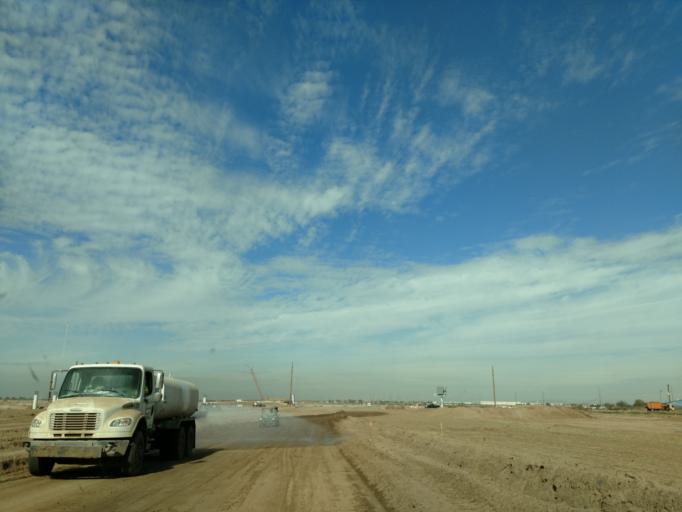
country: US
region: Arizona
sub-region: Maricopa County
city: Laveen
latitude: 33.3901
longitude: -112.1913
